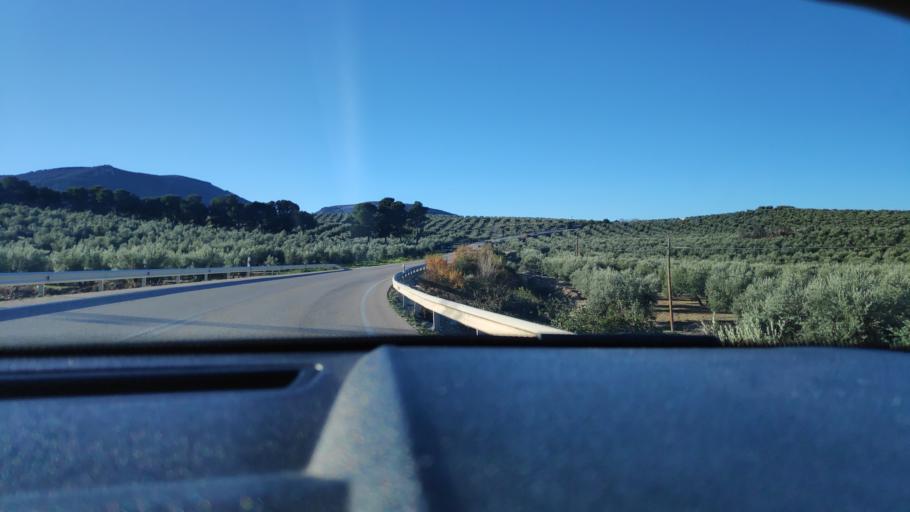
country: ES
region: Andalusia
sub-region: Provincia de Jaen
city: Mancha Real
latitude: 37.8001
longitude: -3.5934
